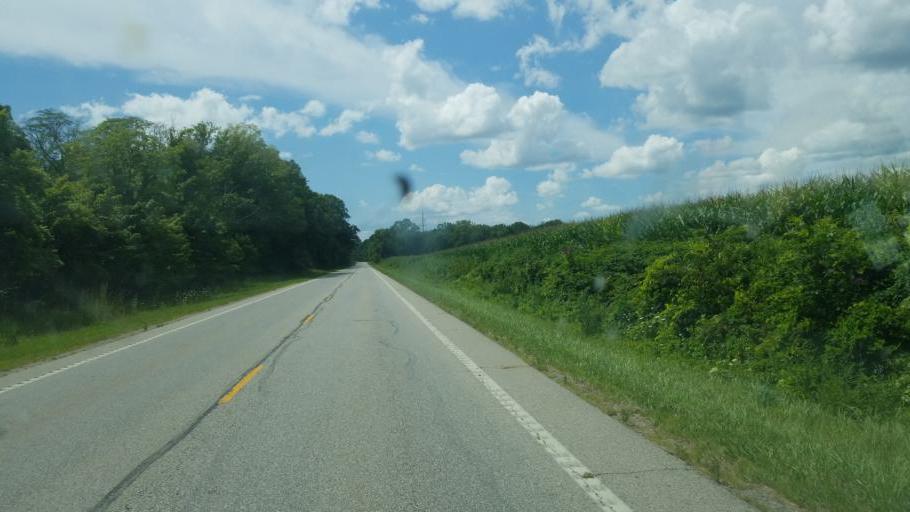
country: US
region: Ohio
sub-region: Delaware County
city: Sunbury
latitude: 40.2508
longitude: -82.8385
